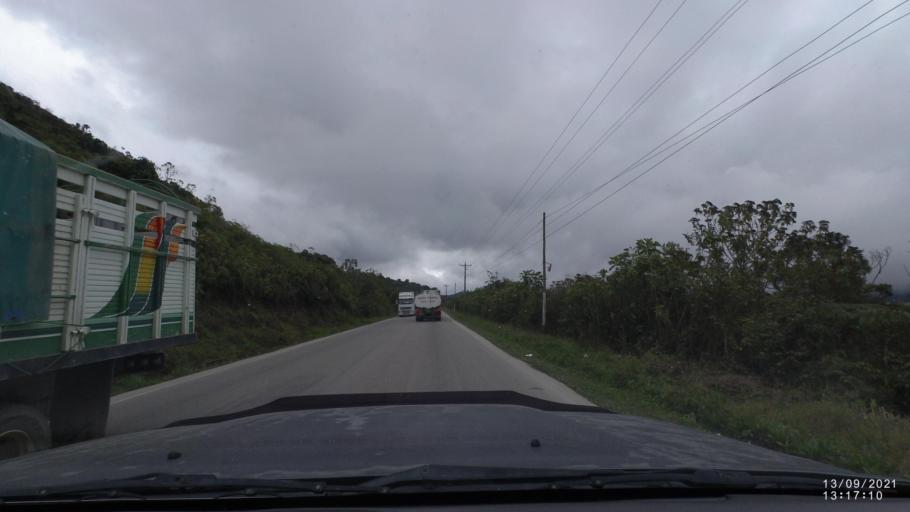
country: BO
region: Cochabamba
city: Colomi
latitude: -17.1998
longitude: -65.8618
